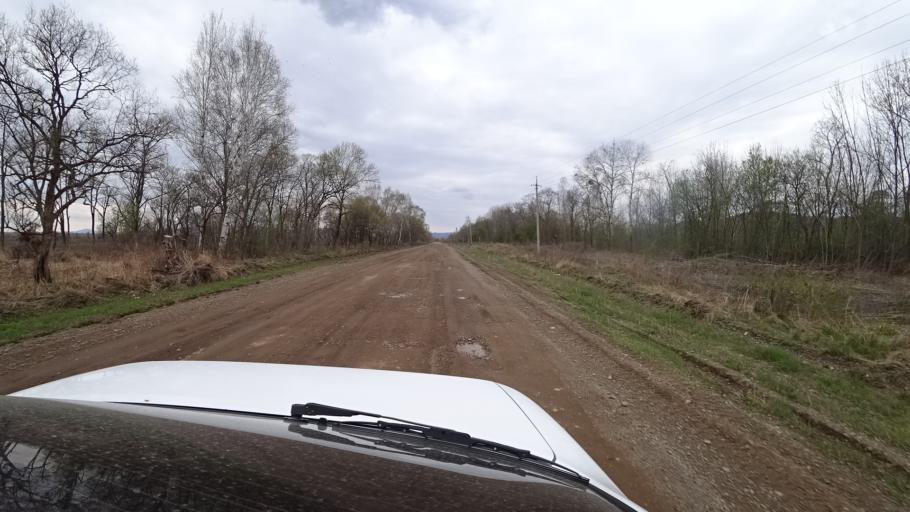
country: RU
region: Primorskiy
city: Novopokrovka
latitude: 45.5592
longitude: 134.3480
